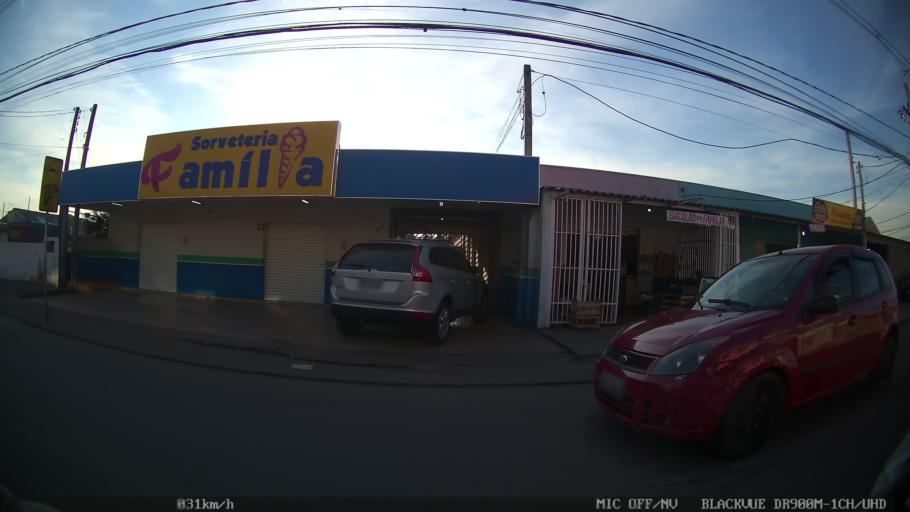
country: BR
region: Parana
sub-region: Pinhais
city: Pinhais
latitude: -25.4497
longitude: -49.1450
